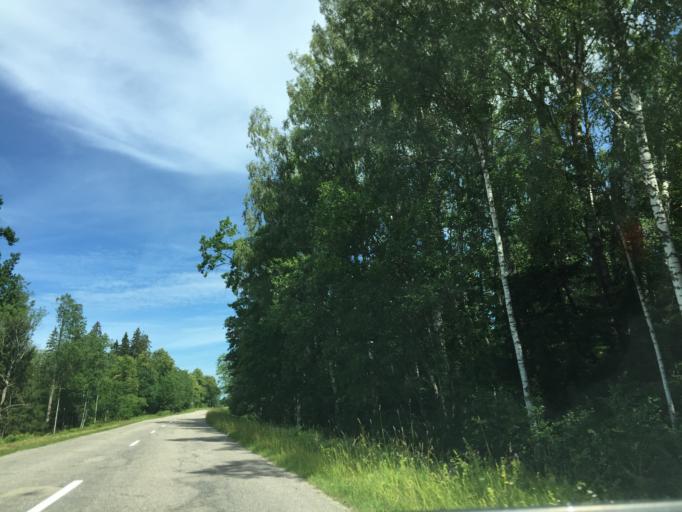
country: LV
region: Dundaga
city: Dundaga
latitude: 57.5693
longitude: 22.3071
